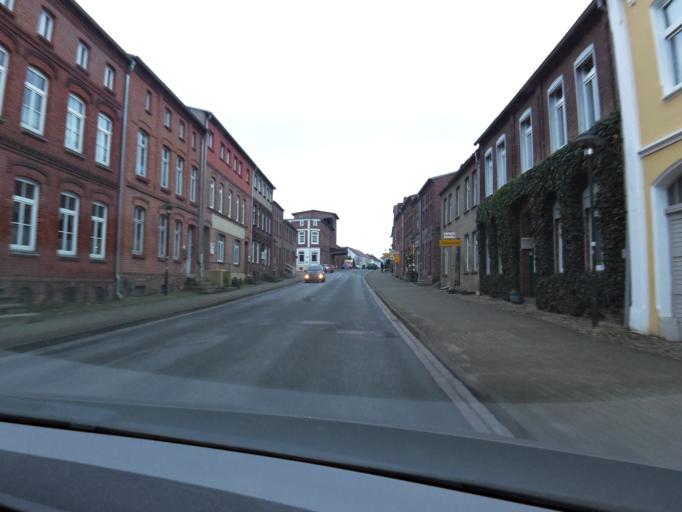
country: DE
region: Mecklenburg-Vorpommern
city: Grevesmuhlen
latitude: 53.8619
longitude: 11.1800
